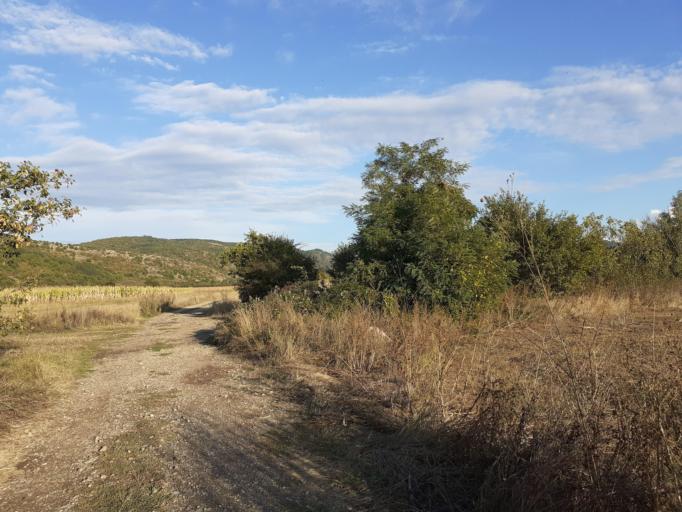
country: RS
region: Central Serbia
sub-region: Pirotski Okrug
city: Dimitrovgrad
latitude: 43.0085
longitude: 22.8183
